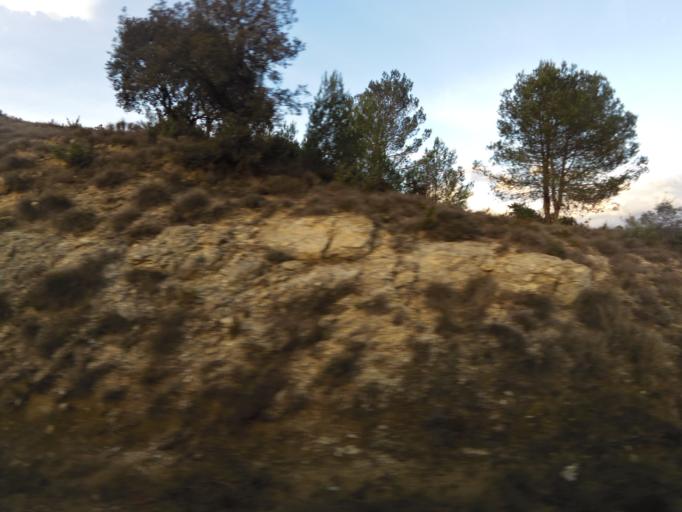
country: FR
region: Languedoc-Roussillon
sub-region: Departement du Gard
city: La Calmette
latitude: 43.8902
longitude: 4.2360
